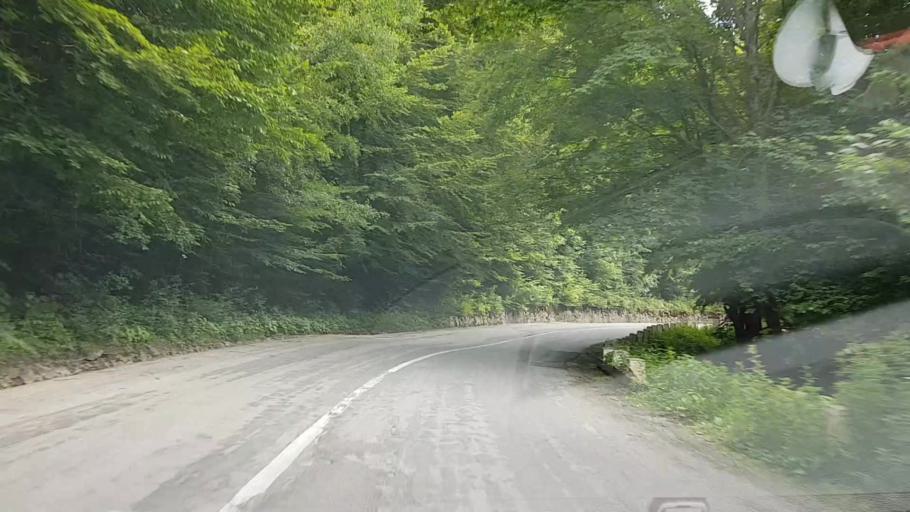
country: RO
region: Neamt
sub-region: Comuna Pangarati
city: Pangarati
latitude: 46.9873
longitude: 26.1177
